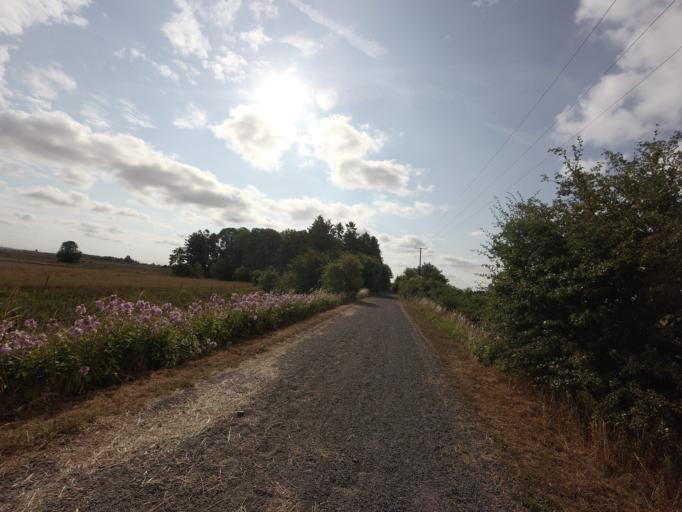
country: SE
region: Skane
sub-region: Angelholms Kommun
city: Strovelstorp
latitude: 56.1507
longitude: 12.7677
